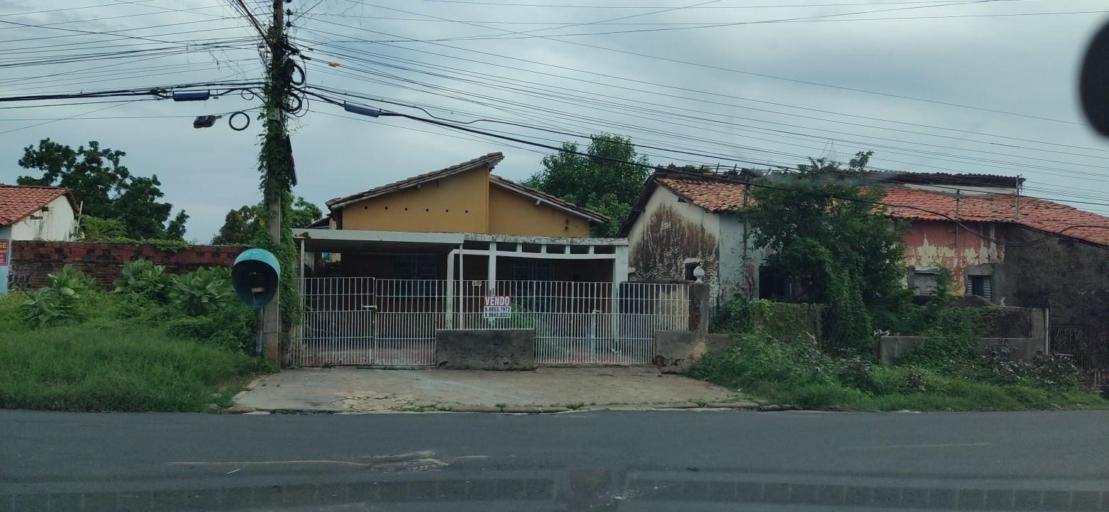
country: BR
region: Piaui
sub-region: Teresina
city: Teresina
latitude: -5.0976
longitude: -42.7988
